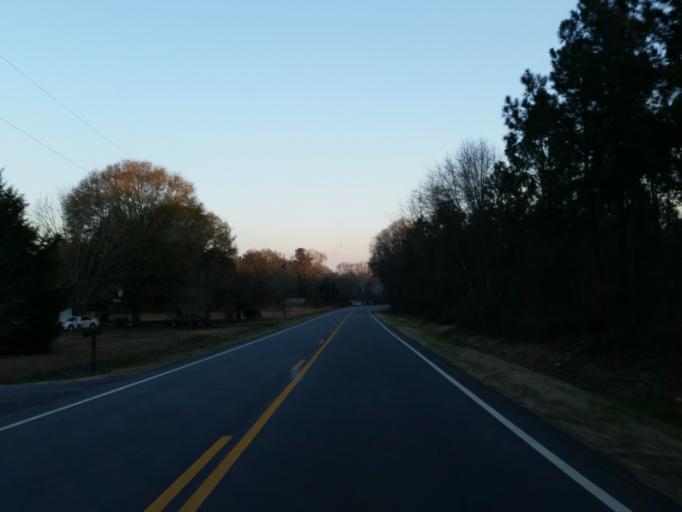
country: US
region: Georgia
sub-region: Turner County
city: Ashburn
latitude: 31.7682
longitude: -83.6874
